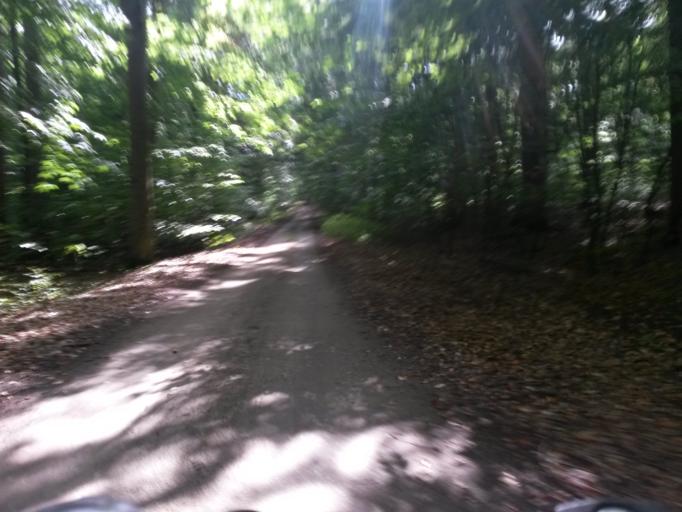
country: DE
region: Brandenburg
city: Templin
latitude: 53.0908
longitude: 13.5319
